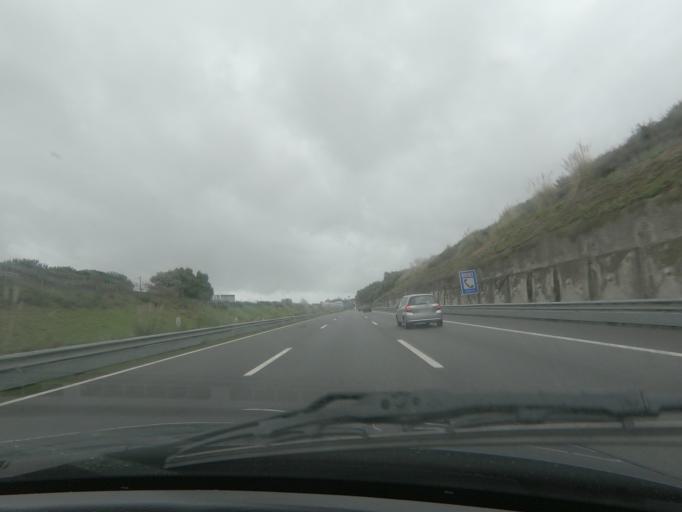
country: PT
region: Porto
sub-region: Matosinhos
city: Santa Cruz do Bispo
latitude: 41.2296
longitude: -8.6778
